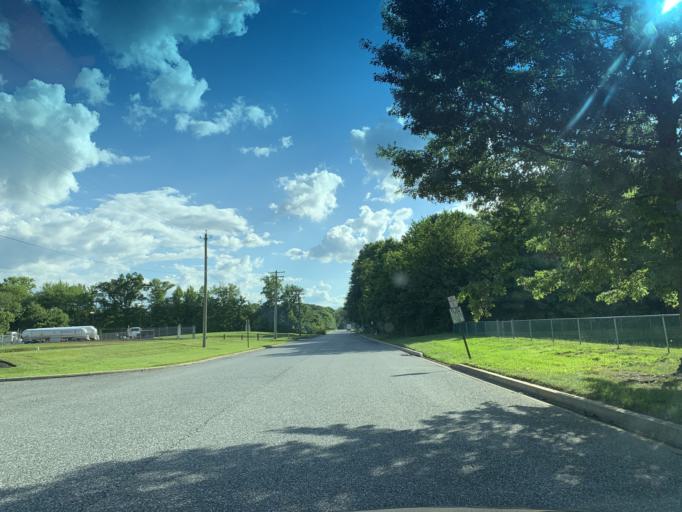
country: US
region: Maryland
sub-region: Harford County
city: Havre de Grace
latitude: 39.5330
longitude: -76.1101
